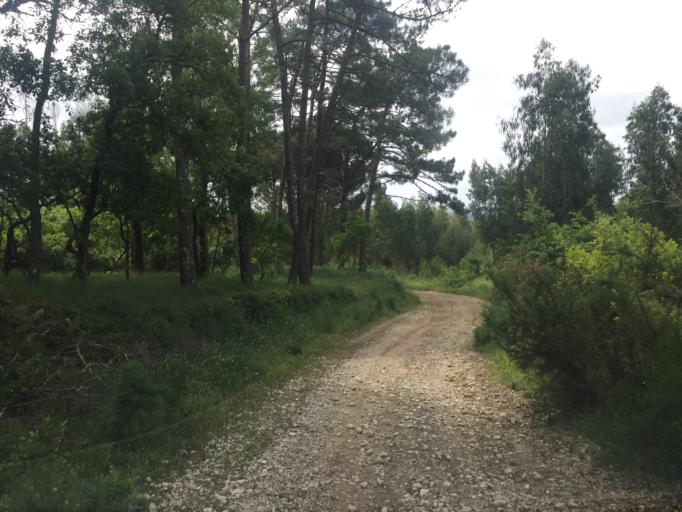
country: PT
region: Coimbra
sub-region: Figueira da Foz
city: Tavarede
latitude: 40.1853
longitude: -8.8225
